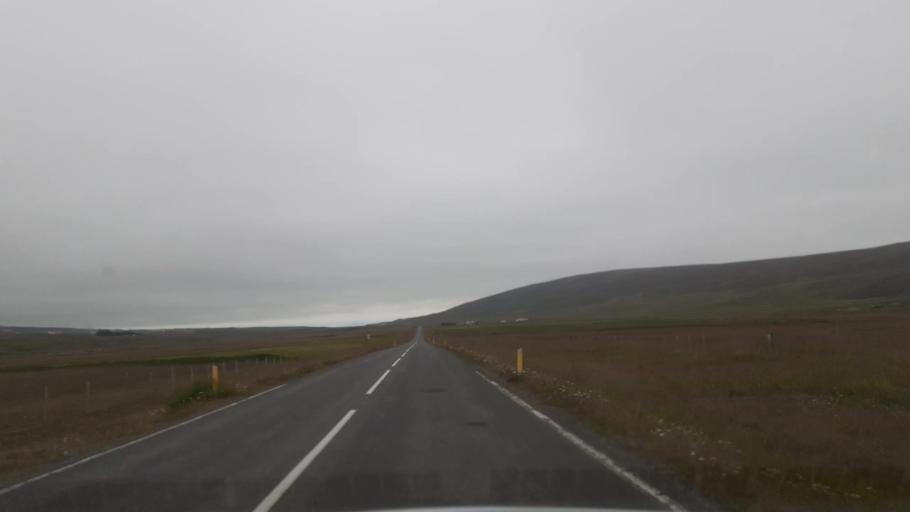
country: IS
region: Northeast
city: Siglufjoerdur
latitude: 65.7412
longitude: -19.1432
